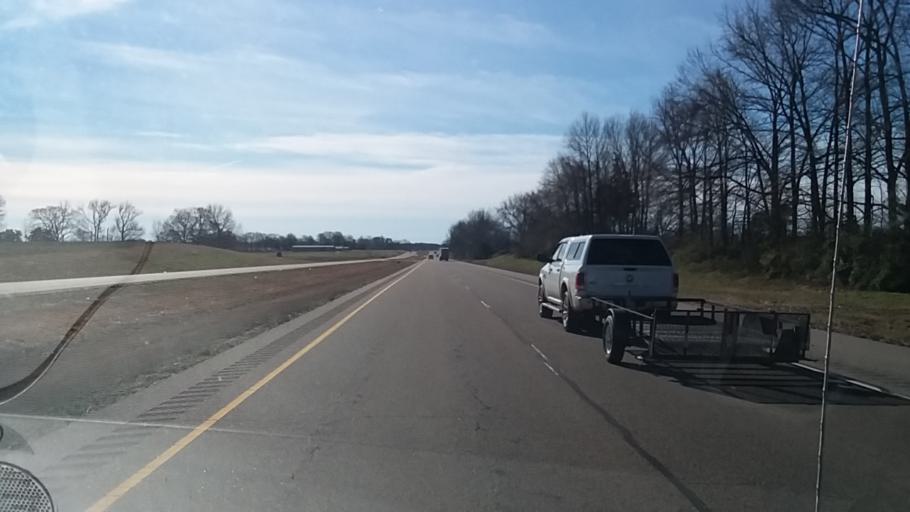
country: US
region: Tennessee
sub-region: Crockett County
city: Alamo
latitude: 35.8671
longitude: -89.2120
